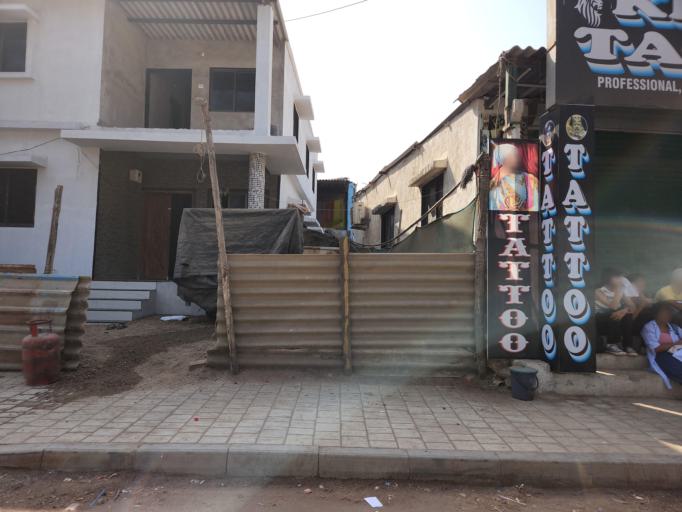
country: IN
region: Daman and Diu
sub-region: Daman District
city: Daman
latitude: 20.3773
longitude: 72.8243
